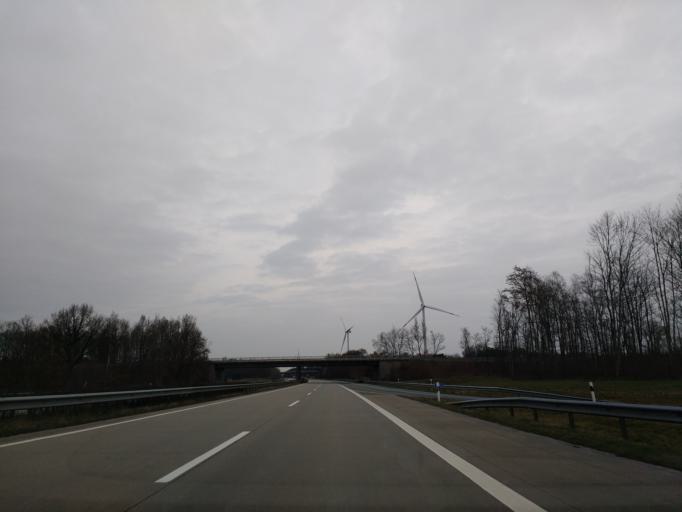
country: DE
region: Lower Saxony
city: Langen
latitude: 53.6203
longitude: 8.6646
